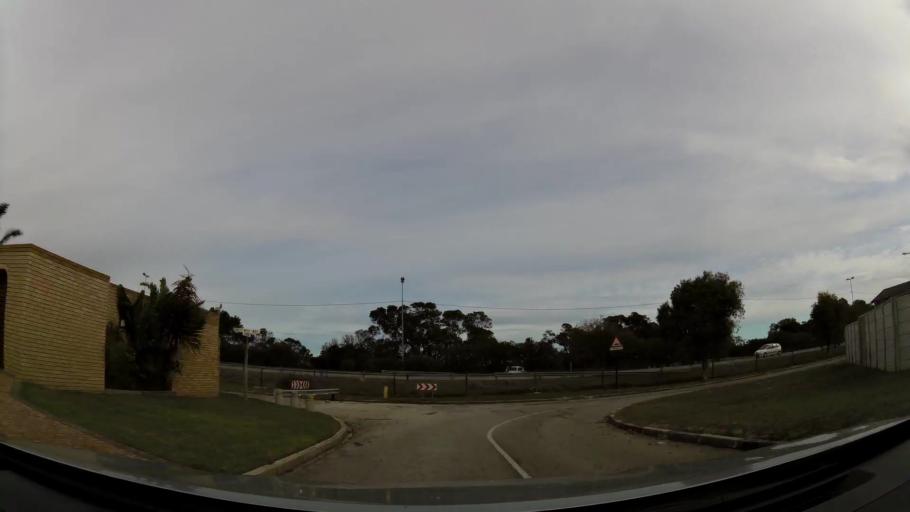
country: ZA
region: Eastern Cape
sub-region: Nelson Mandela Bay Metropolitan Municipality
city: Port Elizabeth
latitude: -33.9451
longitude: 25.4956
